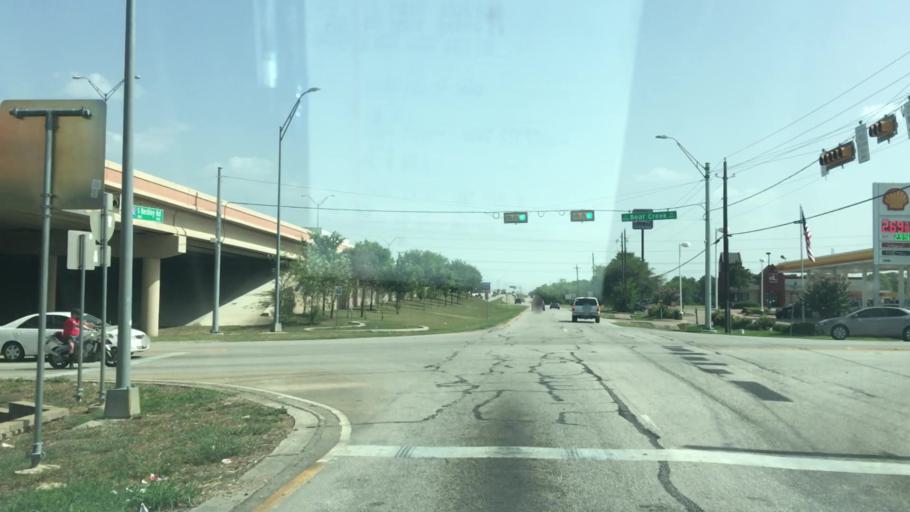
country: US
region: Texas
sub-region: Dallas County
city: Glenn Heights
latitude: 32.5611
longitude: -96.8229
